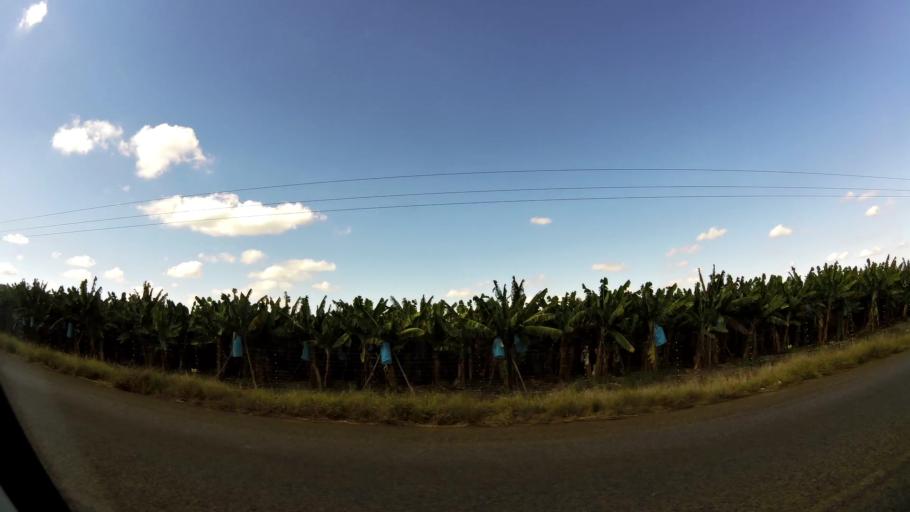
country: ZA
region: Limpopo
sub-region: Mopani District Municipality
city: Tzaneen
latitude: -23.8105
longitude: 30.1749
